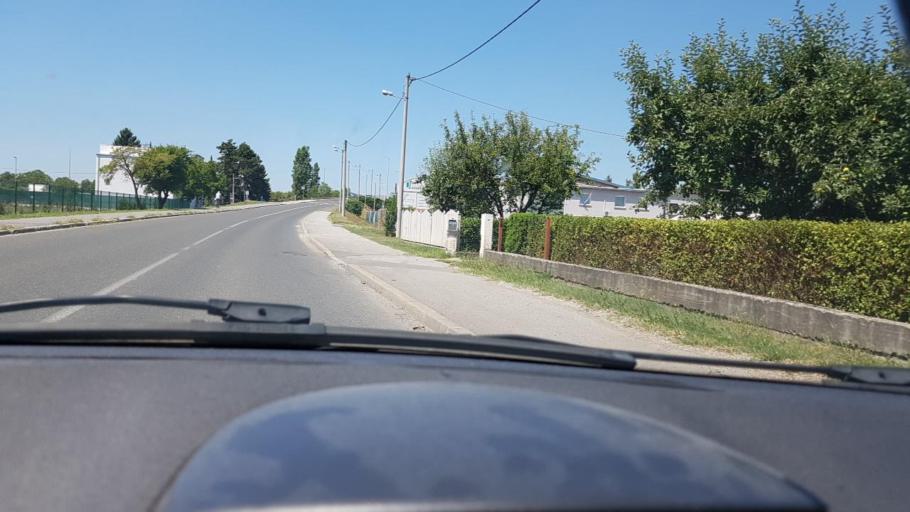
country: HR
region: Grad Zagreb
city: Brezovica
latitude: 45.7505
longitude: 15.8901
